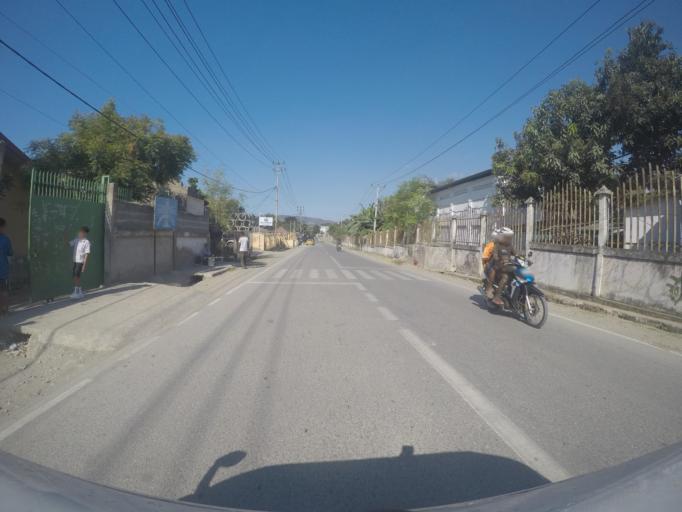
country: TL
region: Dili
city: Dili
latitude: -8.5654
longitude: 125.5550
